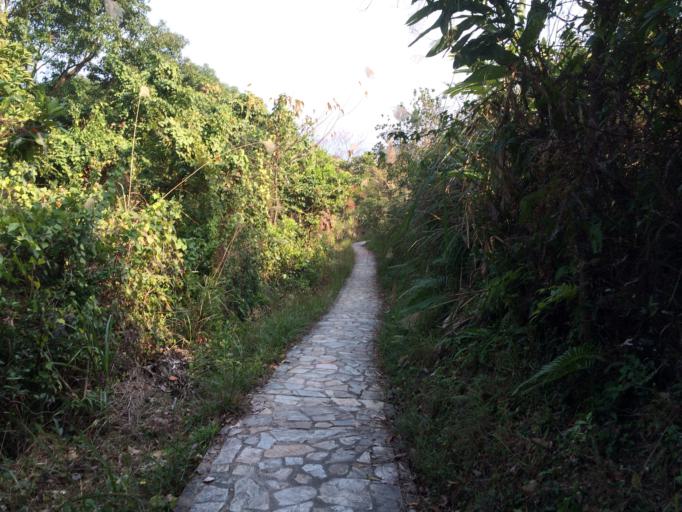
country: HK
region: Tai Po
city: Tai Po
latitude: 22.4514
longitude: 114.2154
